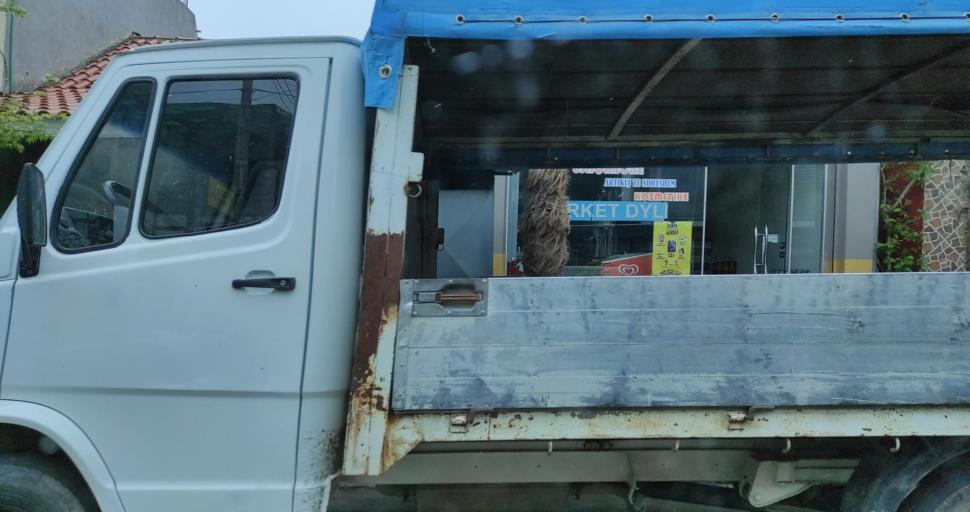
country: AL
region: Shkoder
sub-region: Rrethi i Shkodres
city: Berdica e Madhe
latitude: 41.9796
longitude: 19.4848
